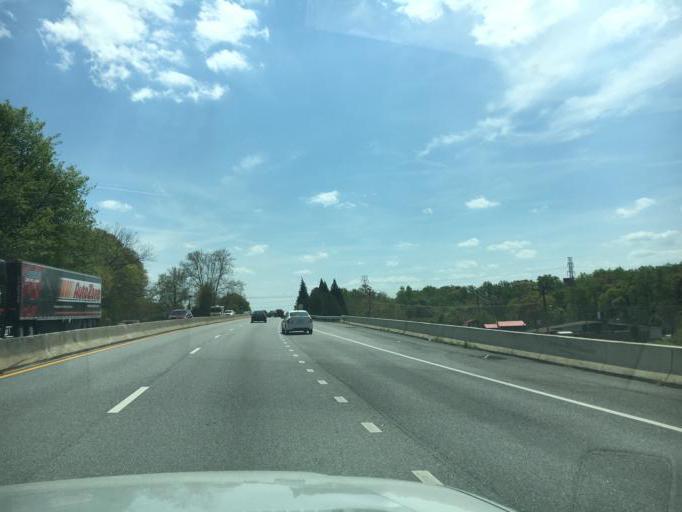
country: US
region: South Carolina
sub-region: Spartanburg County
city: Spartanburg
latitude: 34.9741
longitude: -81.9404
